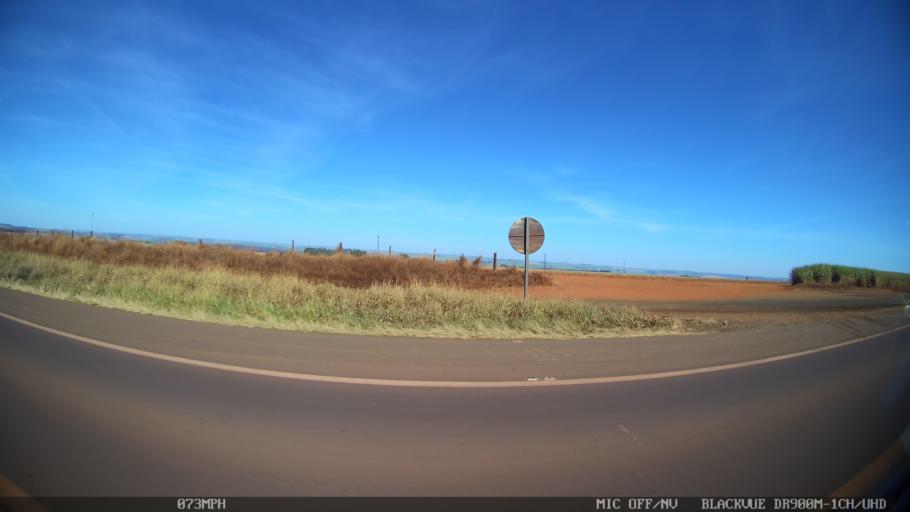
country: BR
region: Sao Paulo
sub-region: Sao Joaquim Da Barra
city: Sao Joaquim da Barra
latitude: -20.5590
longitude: -47.6998
